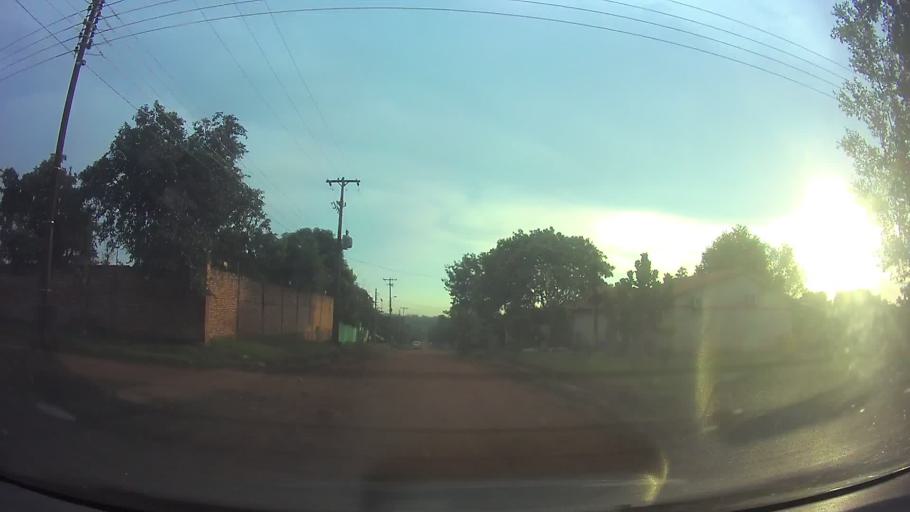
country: PY
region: Central
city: Limpio
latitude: -25.2450
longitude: -57.4552
